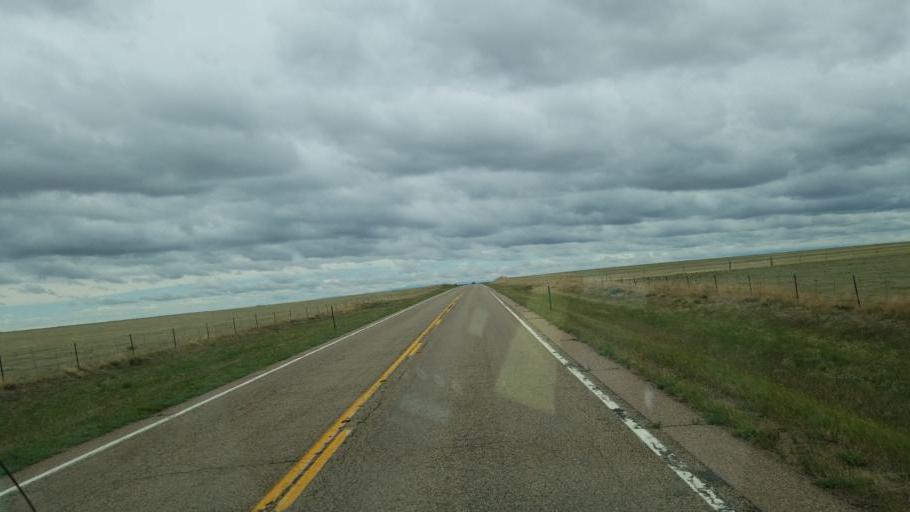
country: US
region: Colorado
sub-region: El Paso County
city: Ellicott
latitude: 38.8393
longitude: -103.9147
